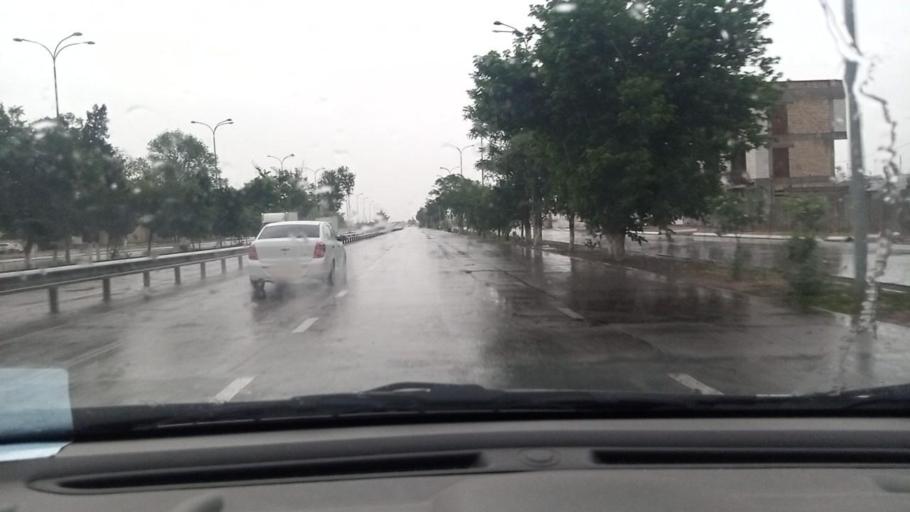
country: UZ
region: Toshkent
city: Ohangaron
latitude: 40.9014
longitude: 69.6505
